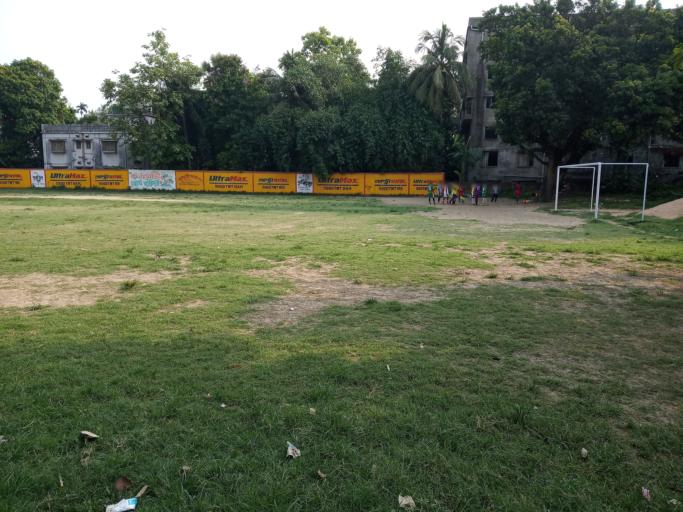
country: IN
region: West Bengal
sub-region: North 24 Parganas
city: Barasat
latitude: 22.7184
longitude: 88.4754
